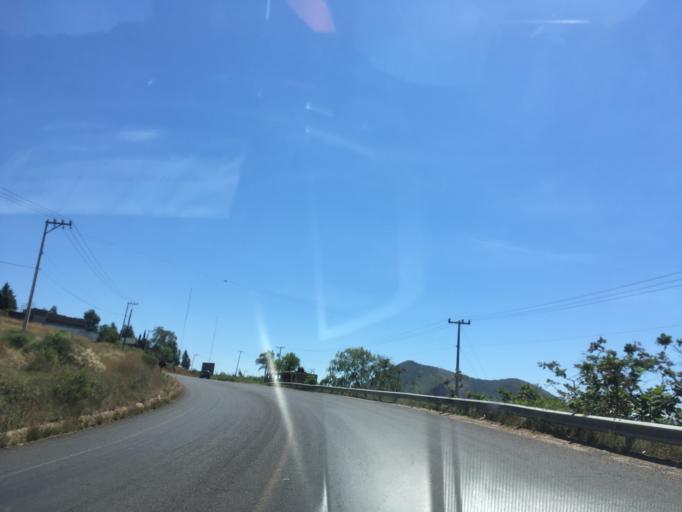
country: MX
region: Michoacan
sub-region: Hidalgo
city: Colonia Aquiles Cordoba Moran
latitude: 19.7081
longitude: -100.5486
